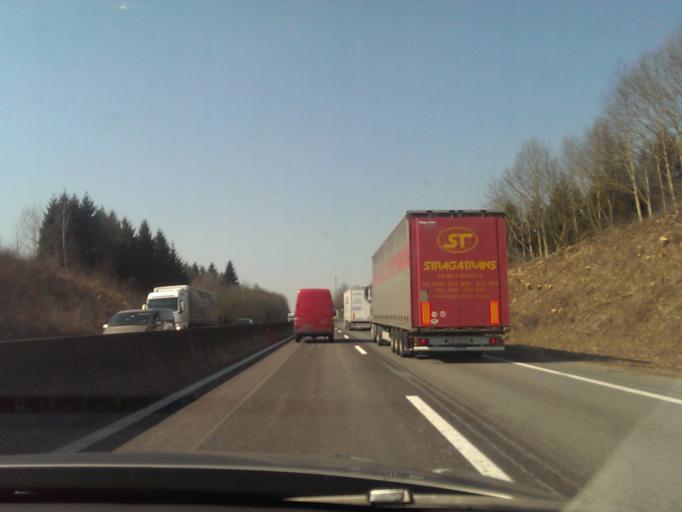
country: AT
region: Upper Austria
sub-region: Politischer Bezirk Ried im Innkreis
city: Ried im Innkreis
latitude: 48.2331
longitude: 13.5894
